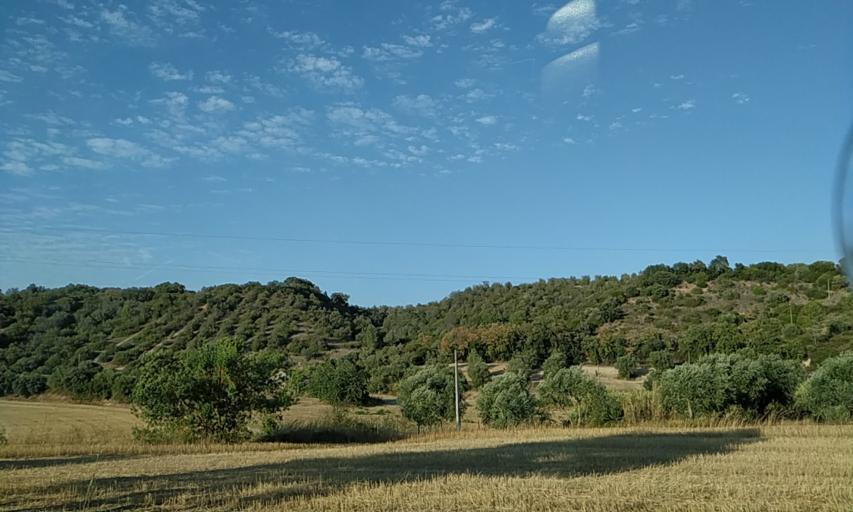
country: PT
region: Santarem
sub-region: Alcanena
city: Alcanena
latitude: 39.3650
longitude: -8.6546
